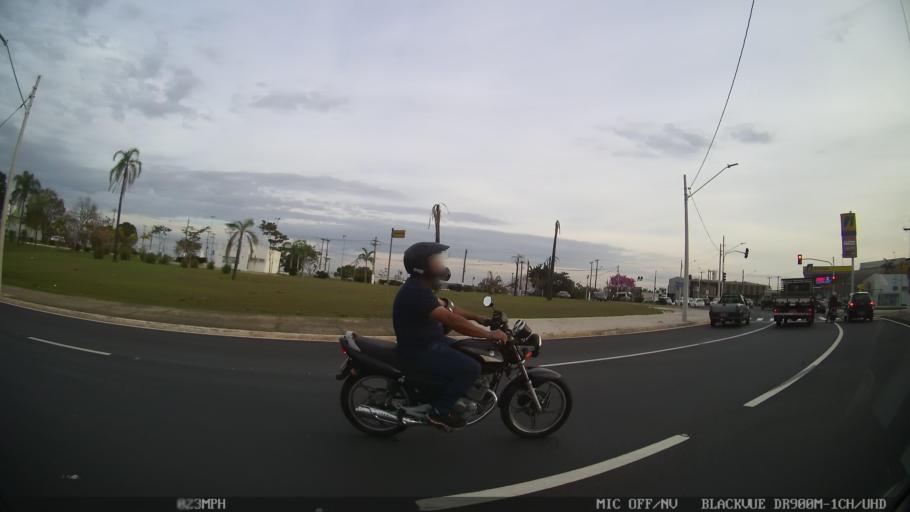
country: BR
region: Sao Paulo
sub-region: Limeira
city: Limeira
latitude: -22.5870
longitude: -47.3739
